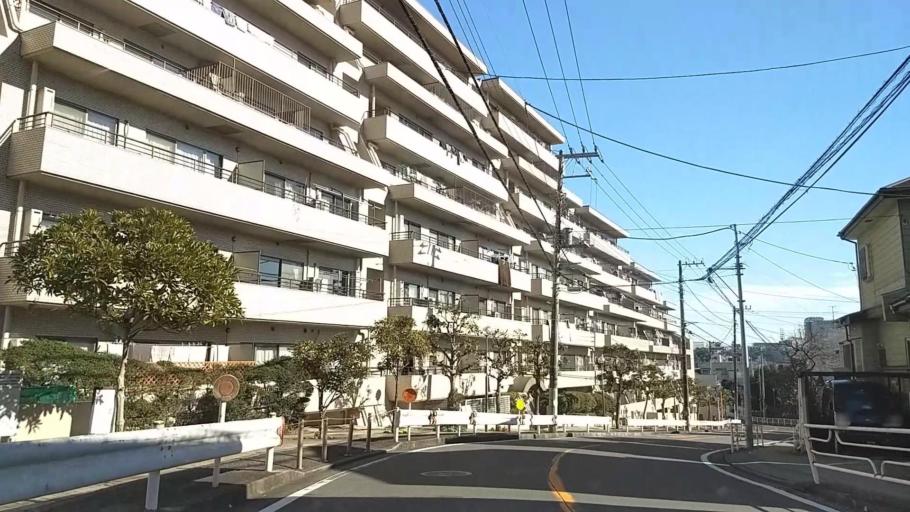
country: JP
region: Kanagawa
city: Yokohama
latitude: 35.4476
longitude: 139.5857
